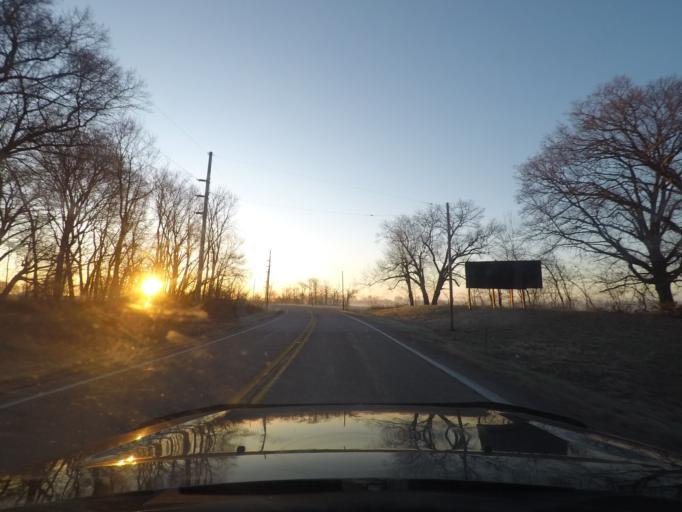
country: US
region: Indiana
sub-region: Saint Joseph County
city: Walkerton
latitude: 41.4482
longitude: -86.4396
